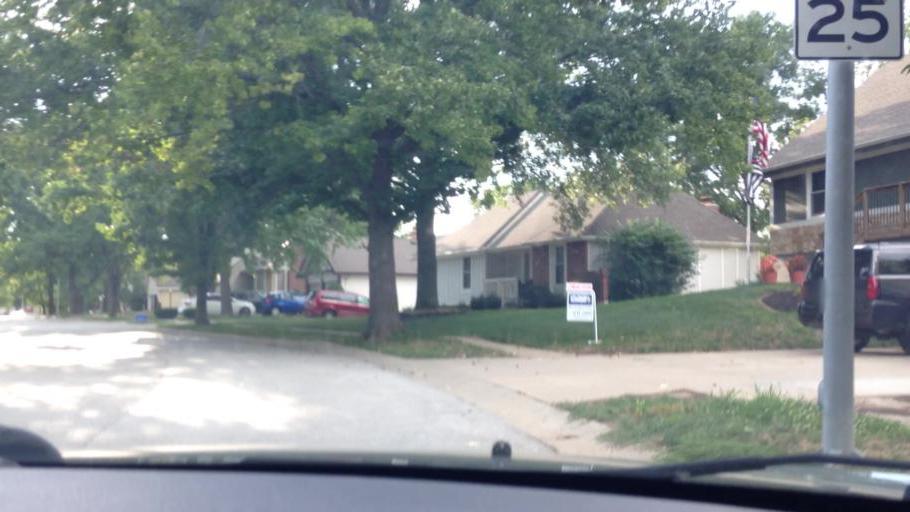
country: US
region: Missouri
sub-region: Platte County
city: Riverside
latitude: 39.2157
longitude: -94.6358
